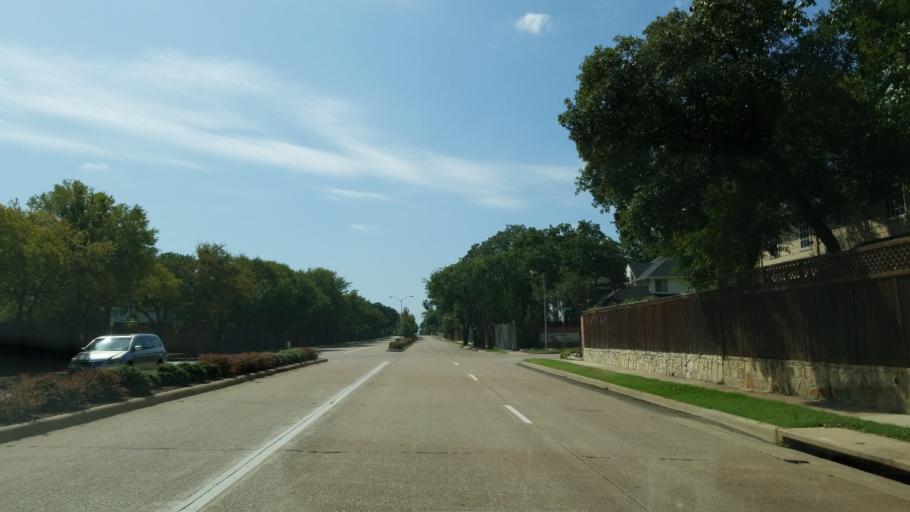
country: US
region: Texas
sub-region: Tarrant County
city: Grapevine
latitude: 32.8874
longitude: -97.0911
